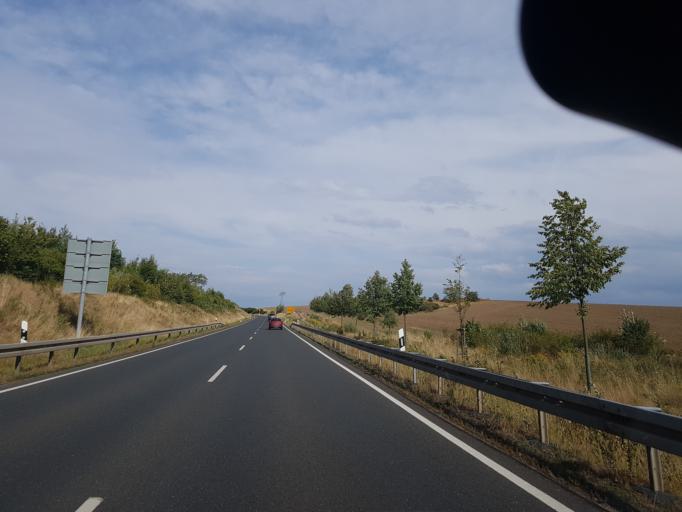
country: DE
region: Saxony
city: Dobeln
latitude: 51.1240
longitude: 13.0809
